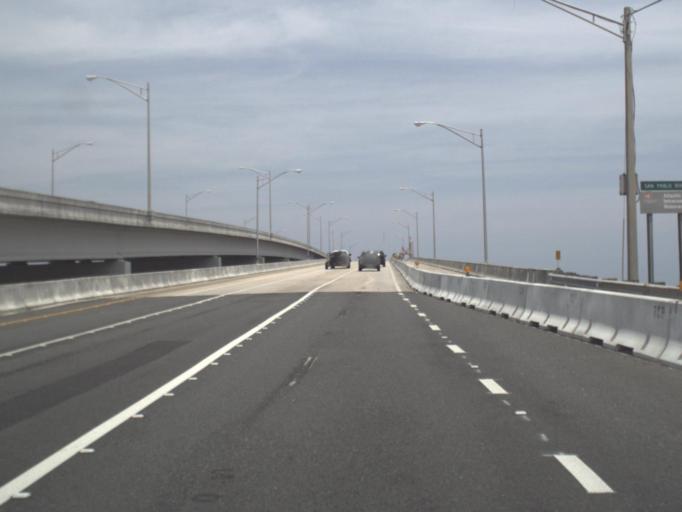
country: US
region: Florida
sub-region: Duval County
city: Atlantic Beach
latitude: 30.3227
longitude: -81.4419
